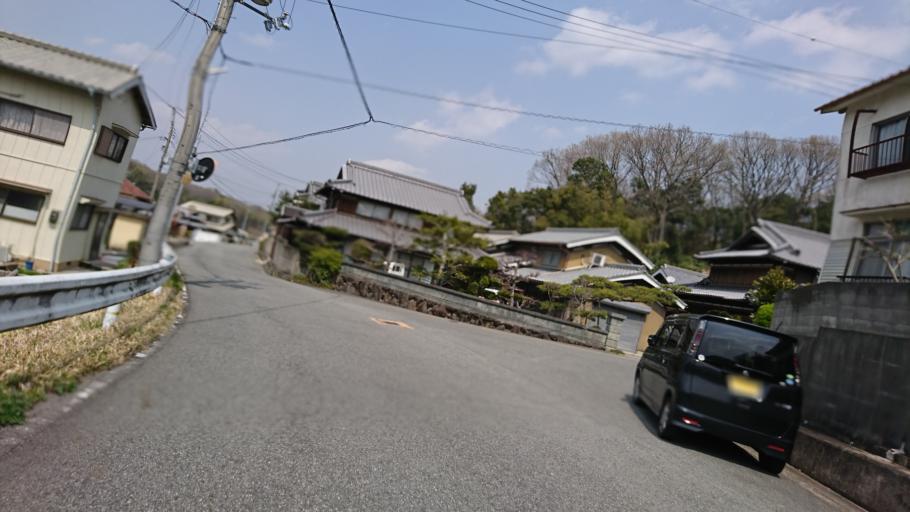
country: JP
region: Hyogo
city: Ono
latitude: 34.8304
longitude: 134.9036
